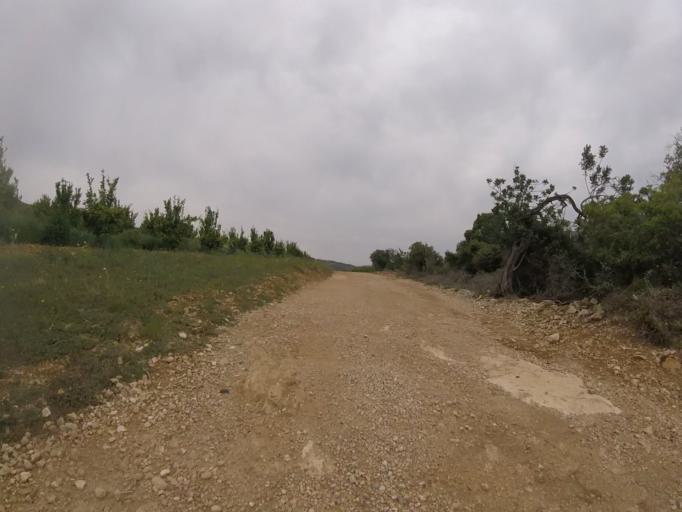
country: ES
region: Valencia
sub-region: Provincia de Castello
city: Alcala de Xivert
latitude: 40.2846
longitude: 0.2568
